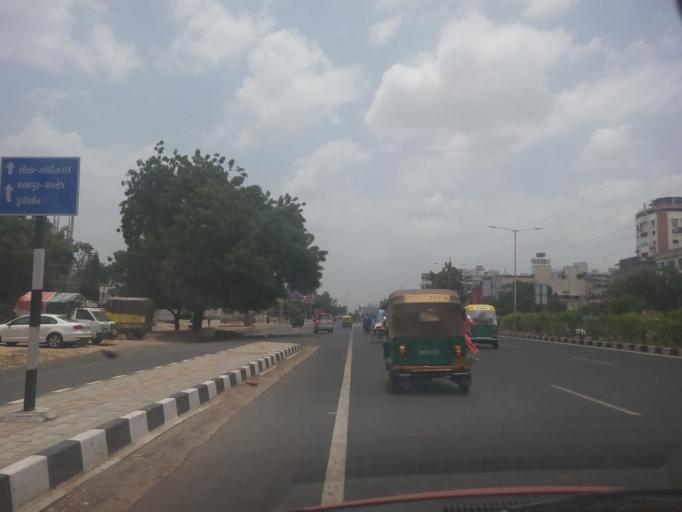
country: IN
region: Gujarat
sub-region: Ahmadabad
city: Sarkhej
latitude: 23.0402
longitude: 72.5125
